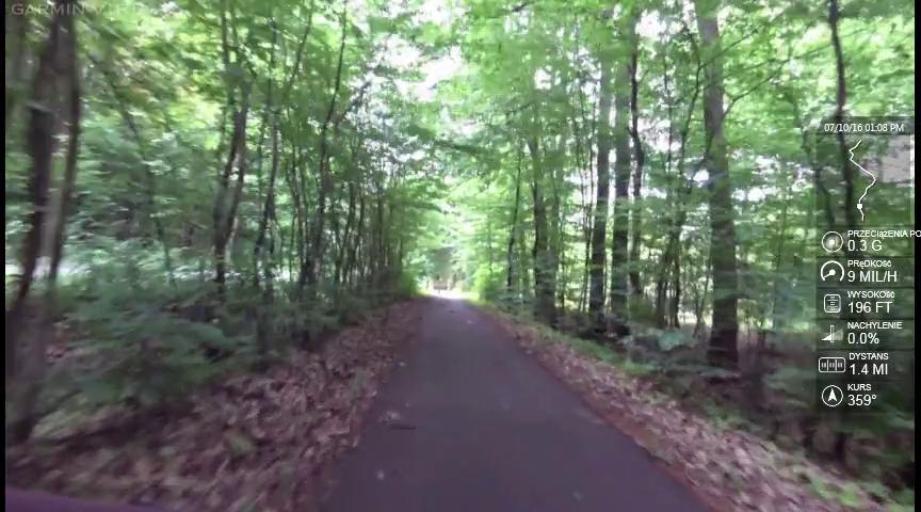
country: PL
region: West Pomeranian Voivodeship
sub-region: Powiat gryfinski
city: Banie
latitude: 53.0581
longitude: 14.6274
